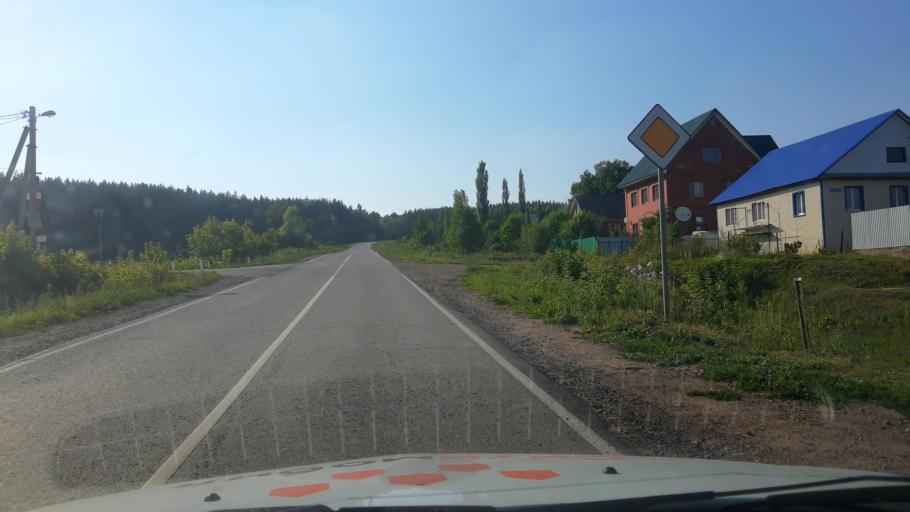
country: RU
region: Bashkortostan
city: Avdon
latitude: 54.6195
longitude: 55.6351
